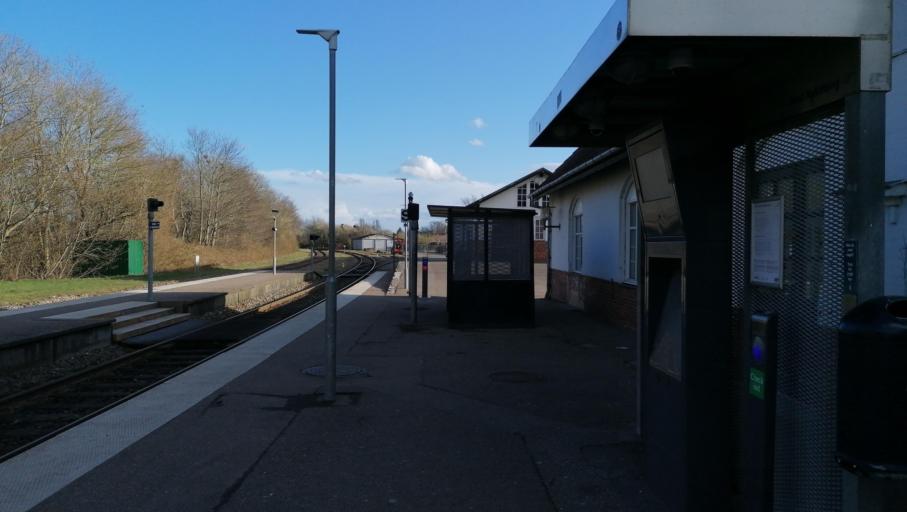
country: DK
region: Zealand
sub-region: Odsherred Kommune
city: Horve
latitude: 55.7526
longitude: 11.4563
